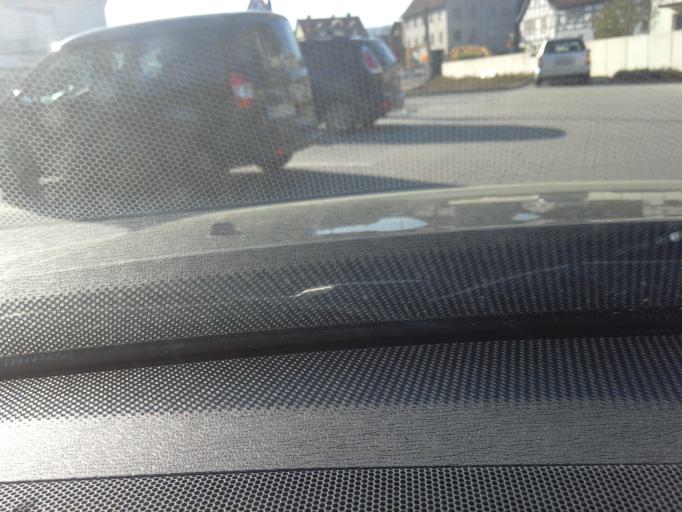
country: DE
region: Hesse
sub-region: Regierungsbezirk Darmstadt
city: Bad Soden-Salmunster
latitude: 50.2783
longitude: 9.3682
